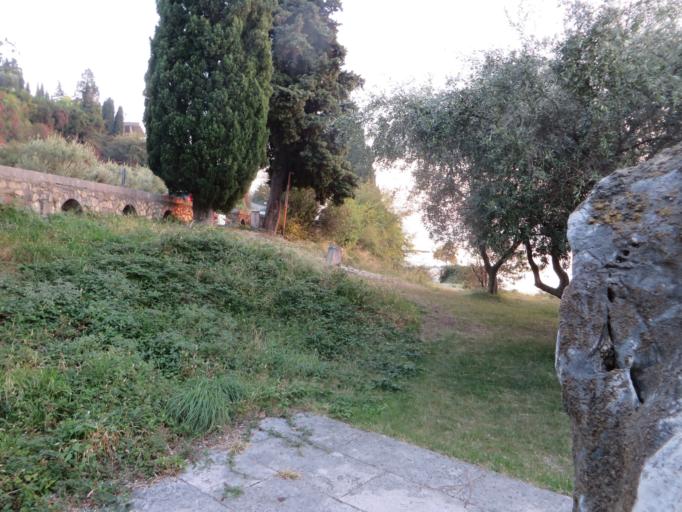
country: IT
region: Veneto
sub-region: Provincia di Verona
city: Torri del Benaco
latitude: 45.5863
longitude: 10.6747
